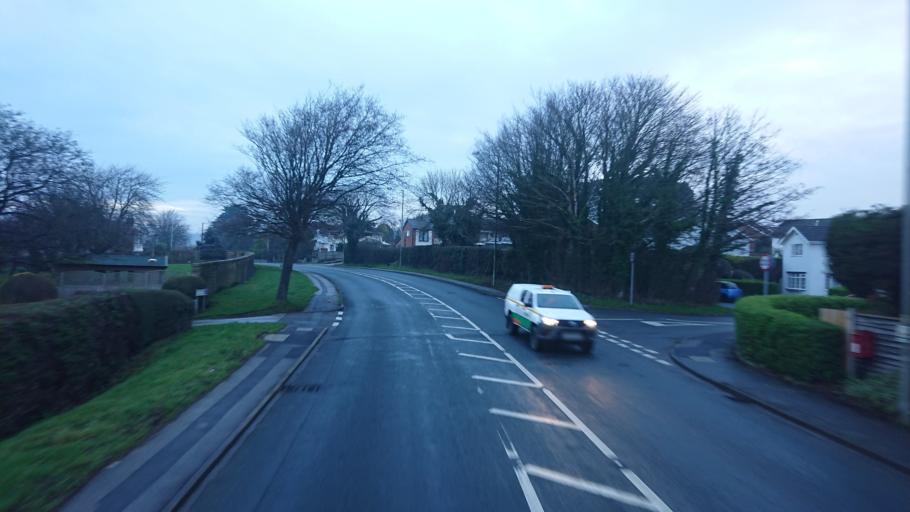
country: GB
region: England
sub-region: Lancashire
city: Bolton le Sands
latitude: 54.0951
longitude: -2.8045
